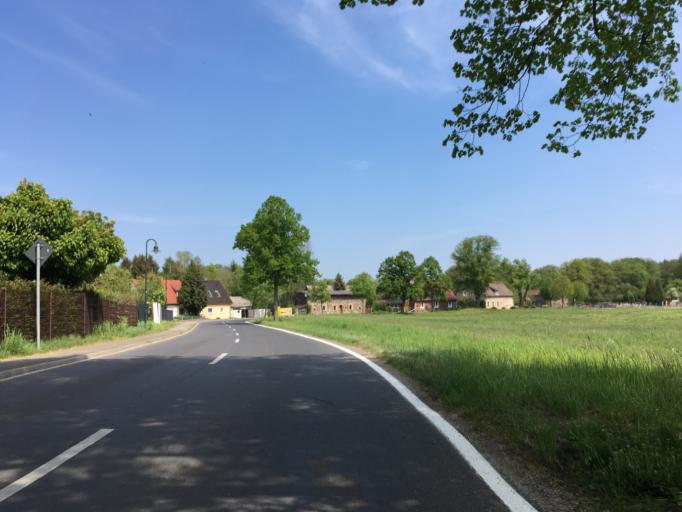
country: DE
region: Brandenburg
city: Melchow
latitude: 52.7355
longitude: 13.7097
